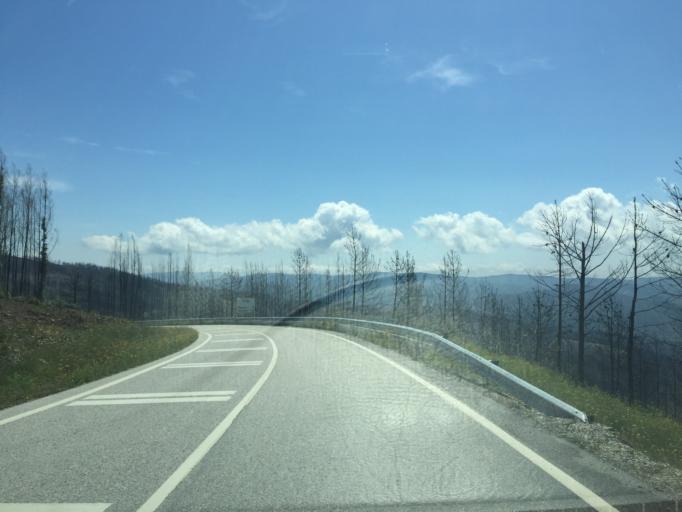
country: PT
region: Coimbra
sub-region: Pampilhosa da Serra
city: Pampilhosa da Serra
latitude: 40.0060
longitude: -7.9918
